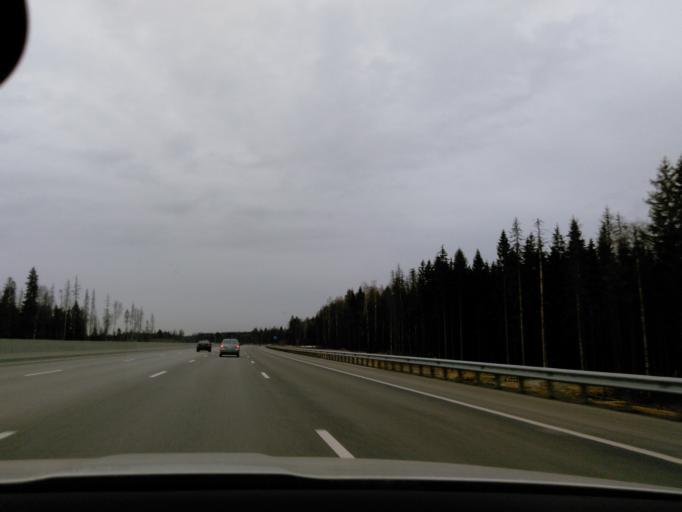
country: RU
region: Moskovskaya
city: Skhodnya
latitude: 55.9917
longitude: 37.3023
